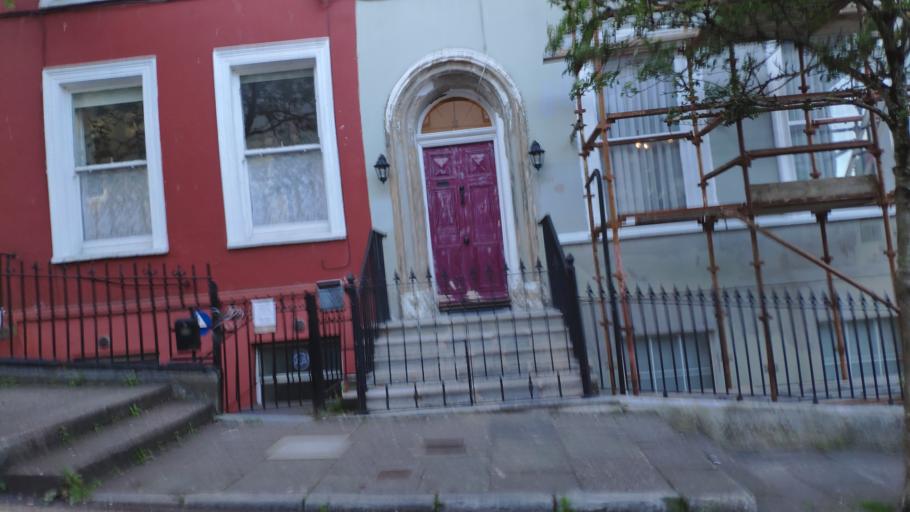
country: IE
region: Munster
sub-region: County Cork
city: Cork
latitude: 51.9022
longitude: -8.4700
